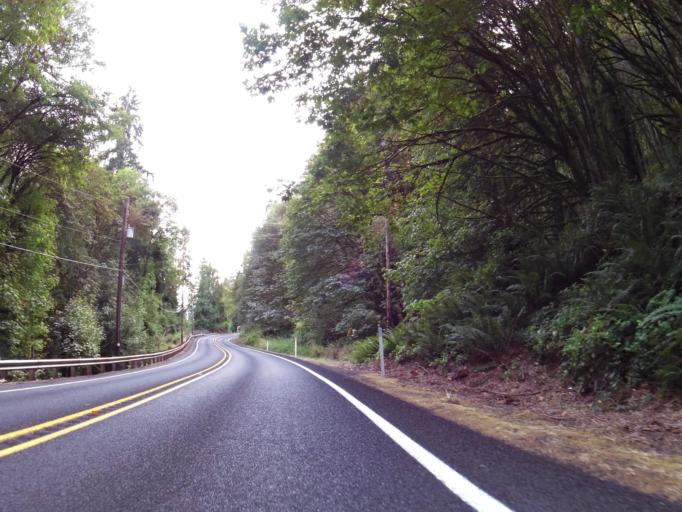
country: US
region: Oregon
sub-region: Columbia County
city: Clatskanie
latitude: 46.1721
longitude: -123.2335
